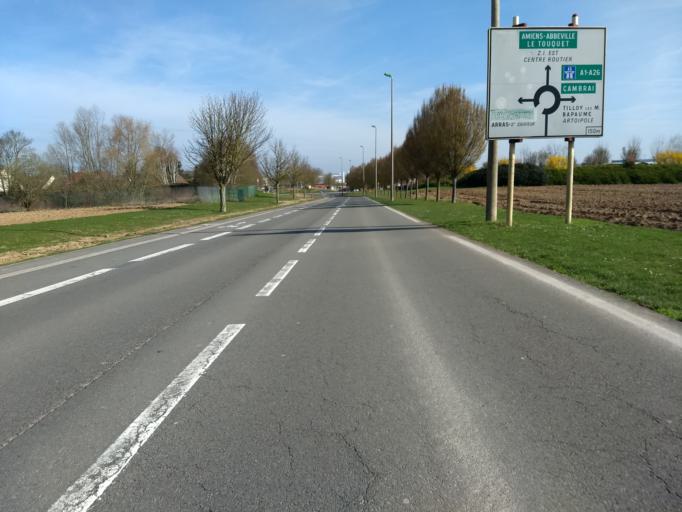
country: FR
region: Nord-Pas-de-Calais
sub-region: Departement du Pas-de-Calais
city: Tilloy-les-Mofflaines
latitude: 50.2807
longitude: 2.8017
